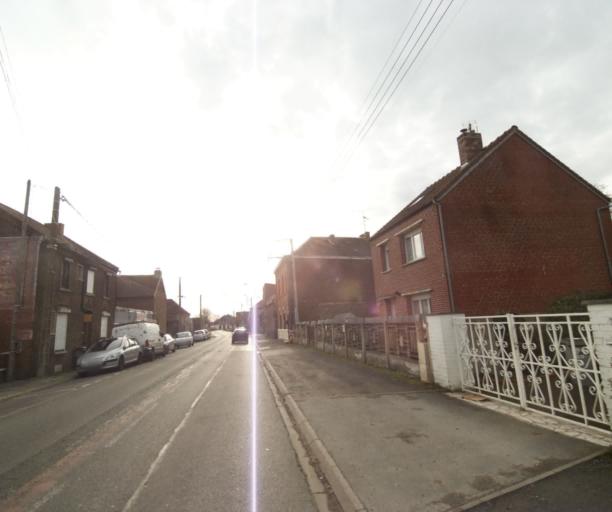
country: FR
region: Nord-Pas-de-Calais
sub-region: Departement du Nord
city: Vicq
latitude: 50.4110
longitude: 3.6010
